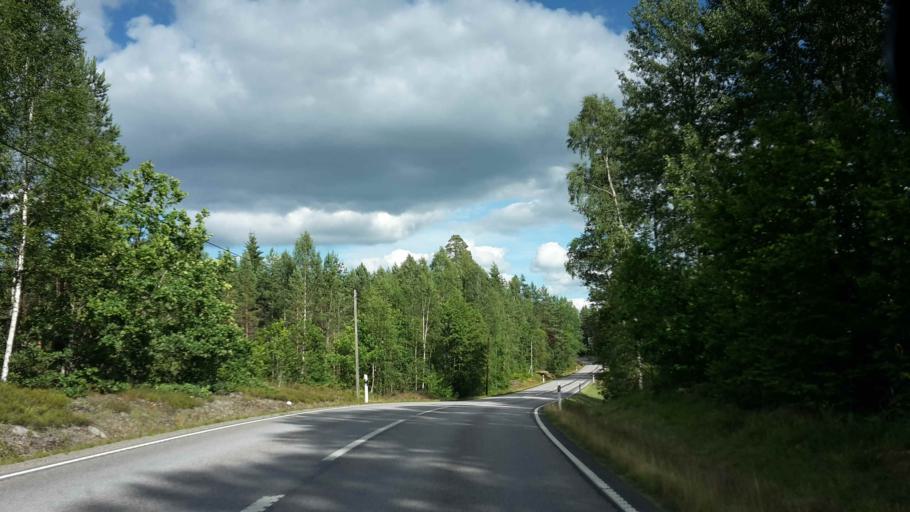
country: SE
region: OEstergoetland
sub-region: Motala Kommun
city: Borensberg
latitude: 58.8021
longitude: 15.4288
